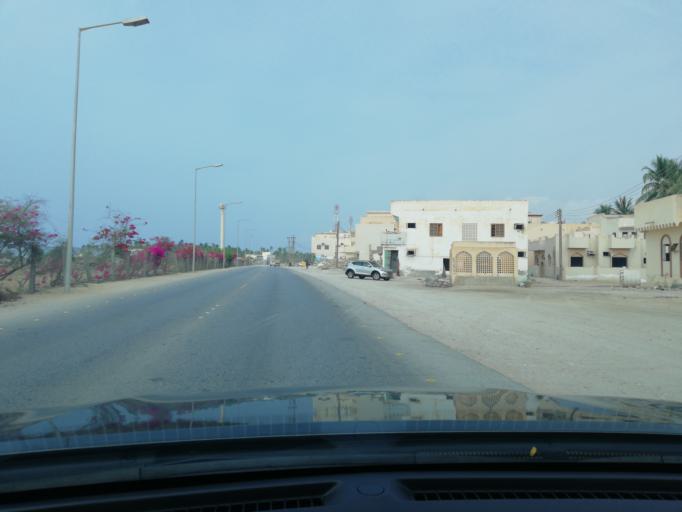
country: OM
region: Zufar
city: Salalah
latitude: 17.0068
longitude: 54.1276
